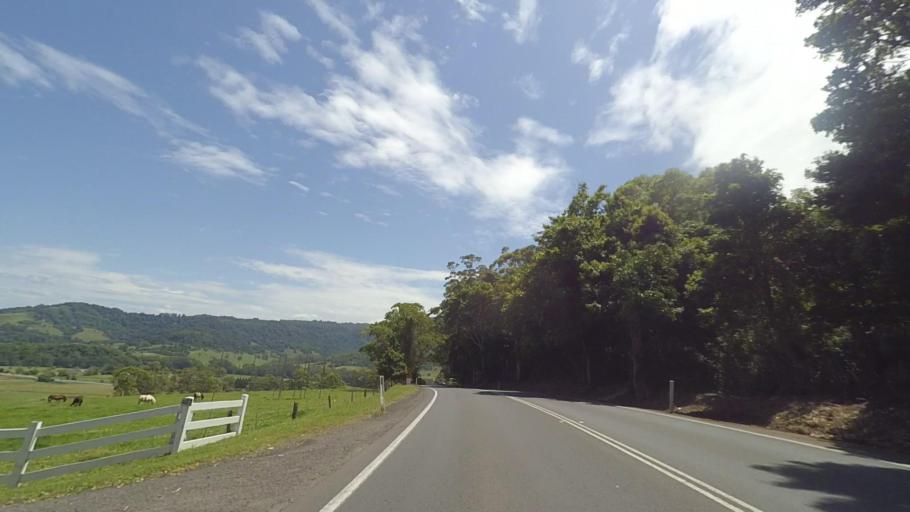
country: AU
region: New South Wales
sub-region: Kiama
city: Gerringong
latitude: -34.7410
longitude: 150.7706
